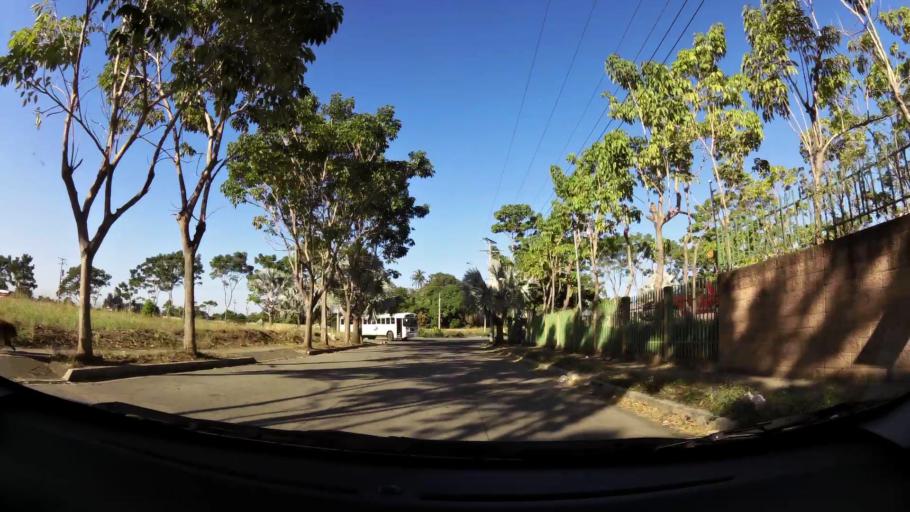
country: SV
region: Sonsonate
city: Sonsonate
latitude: 13.7120
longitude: -89.7192
